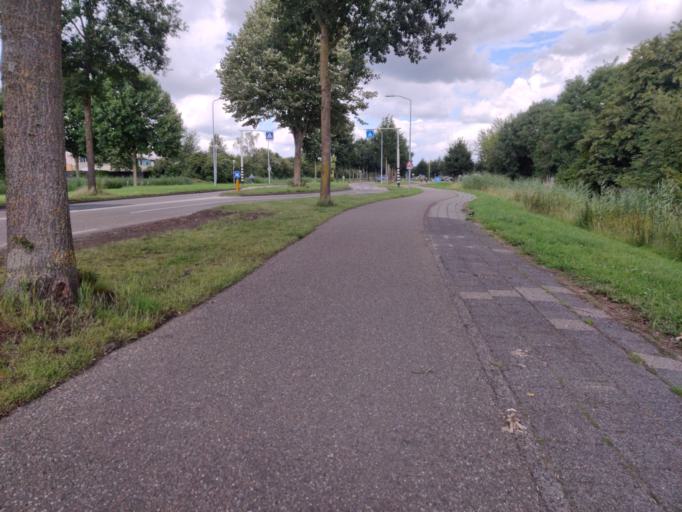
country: NL
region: Flevoland
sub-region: Gemeente Zeewolde
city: Zeewolde
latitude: 52.3345
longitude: 5.5254
